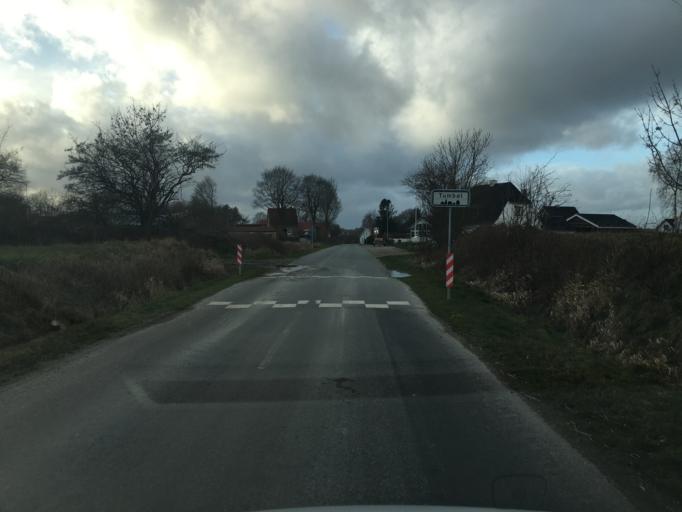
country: DK
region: South Denmark
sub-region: Sonderborg Kommune
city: Grasten
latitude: 54.9699
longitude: 9.5195
